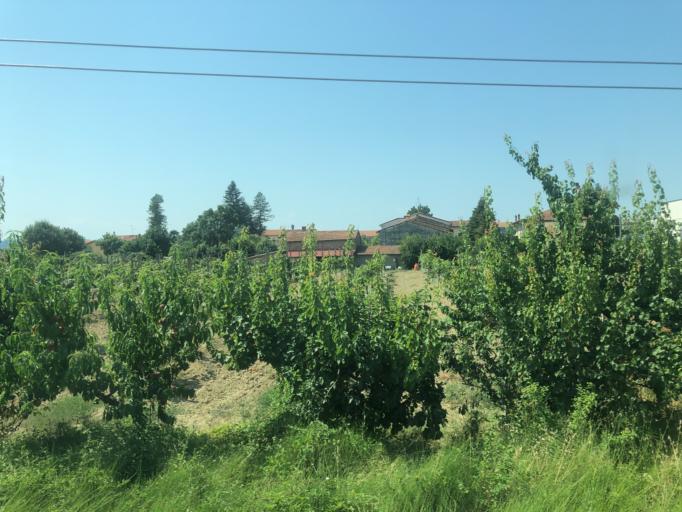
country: IT
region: Emilia-Romagna
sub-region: Provincia di Ravenna
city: Castel Bolognese
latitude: 44.3230
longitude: 11.8100
